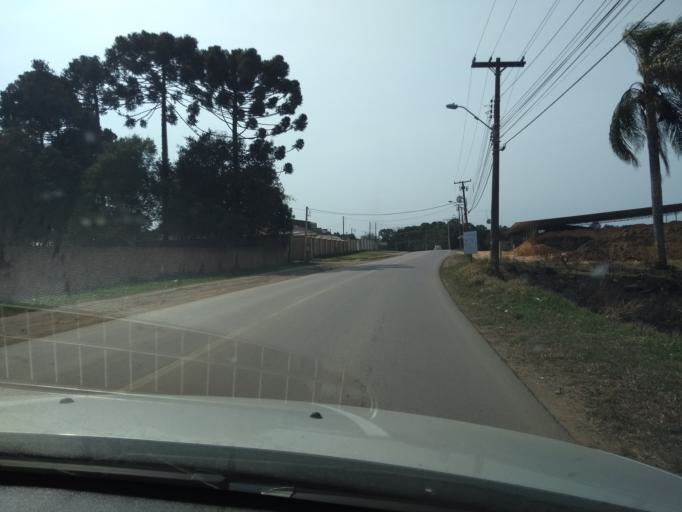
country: BR
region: Parana
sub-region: Araucaria
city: Araucaria
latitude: -25.6075
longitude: -49.3323
